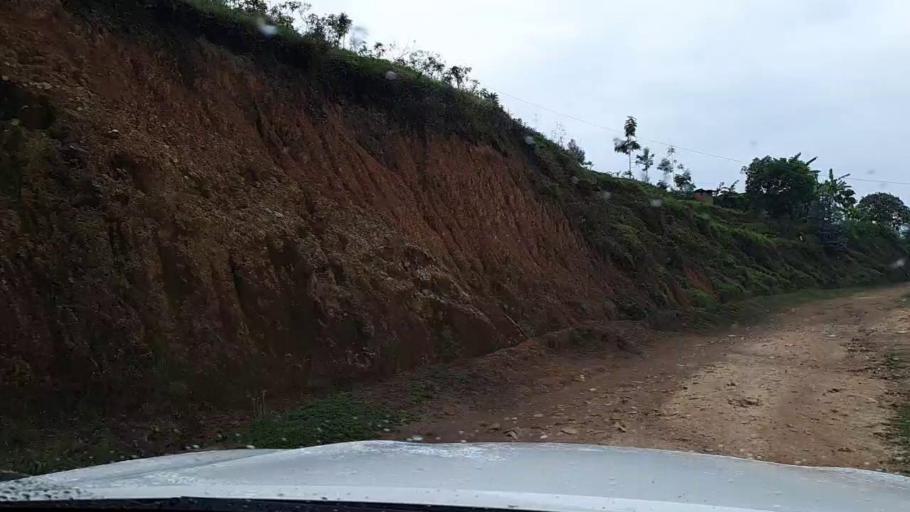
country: RW
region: Southern Province
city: Nzega
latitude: -2.4577
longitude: 29.4926
